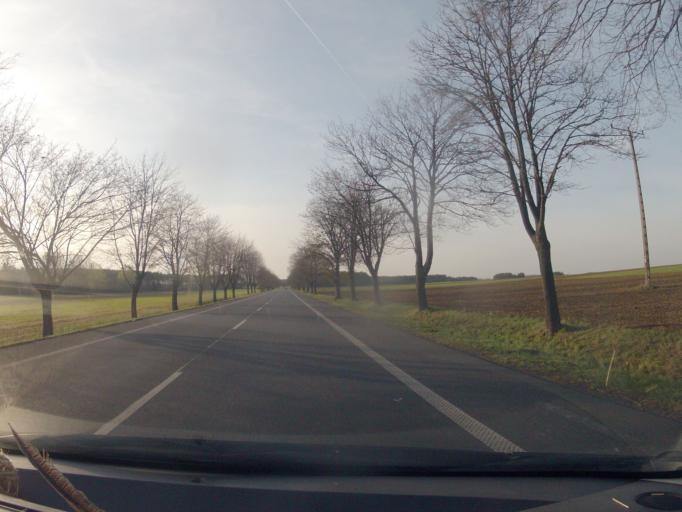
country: PL
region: Opole Voivodeship
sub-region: Powiat strzelecki
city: Izbicko
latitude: 50.5606
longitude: 18.1883
